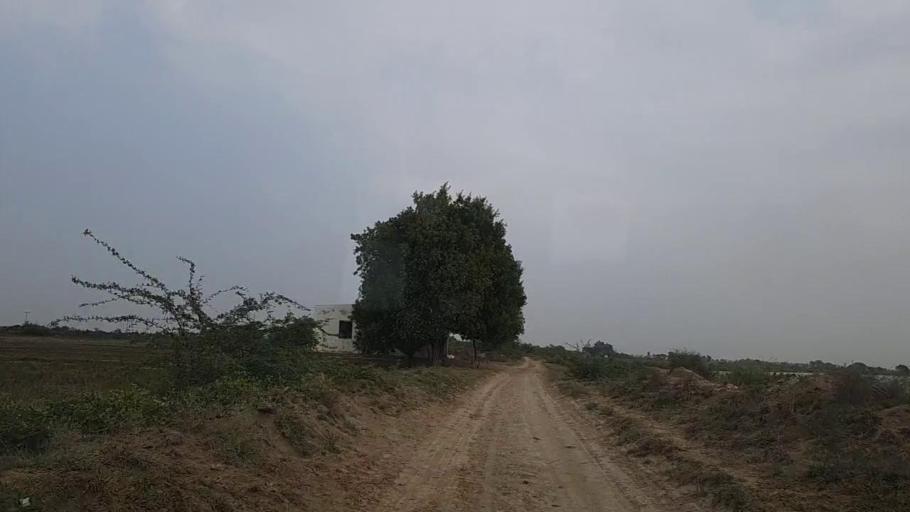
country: PK
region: Sindh
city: Mirpur Sakro
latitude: 24.6070
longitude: 67.7052
